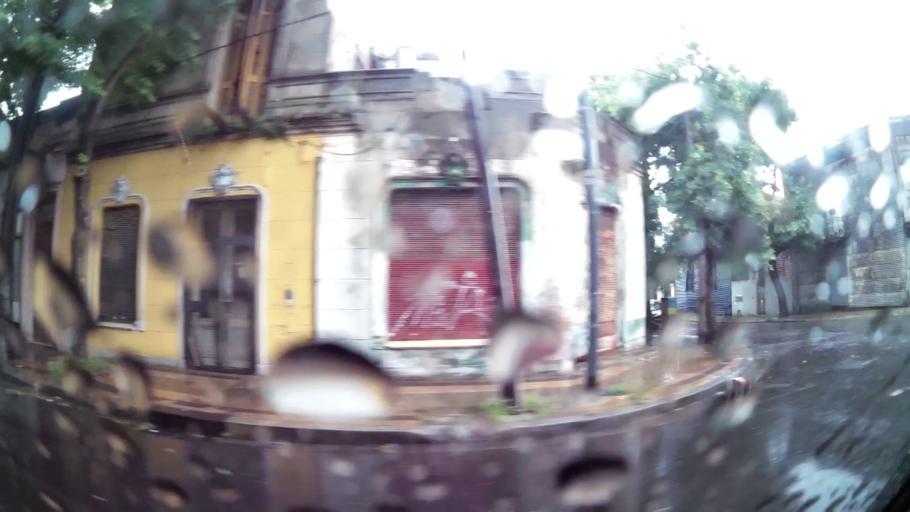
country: AR
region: Buenos Aires
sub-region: Partido de Avellaneda
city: Avellaneda
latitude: -34.6447
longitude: -58.3624
